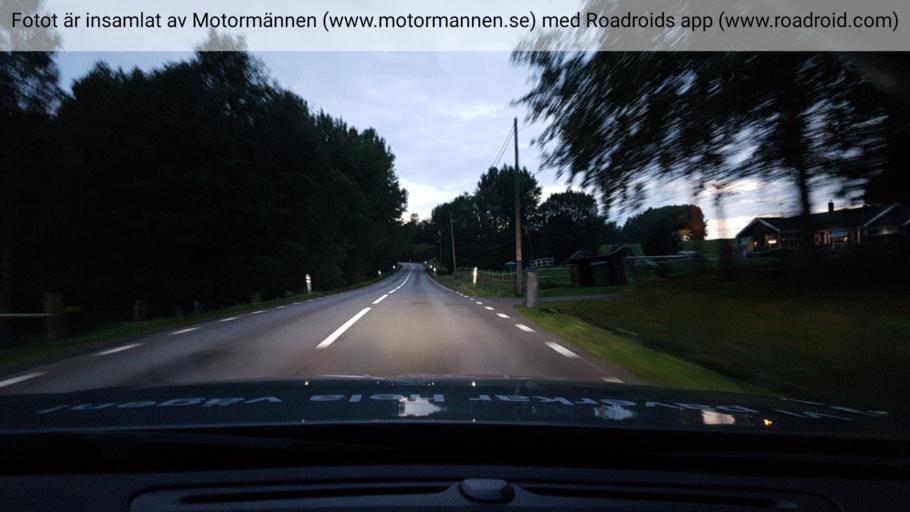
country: SE
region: OErebro
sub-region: Karlskoga Kommun
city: Karlskoga
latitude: 59.3918
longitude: 14.6218
